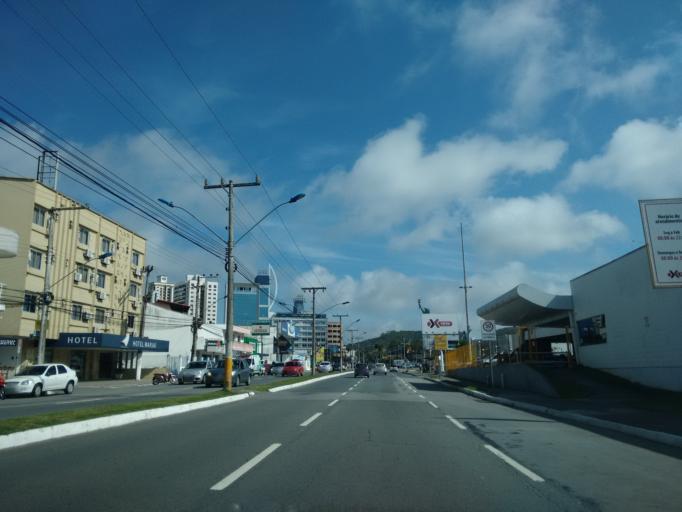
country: BR
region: Santa Catarina
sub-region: Itajai
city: Itajai
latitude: -26.9183
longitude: -48.6546
